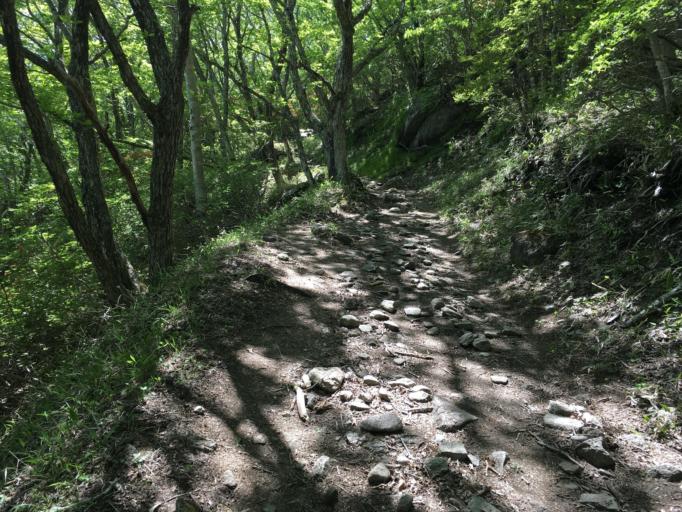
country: JP
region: Iwate
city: Ofunato
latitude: 39.1833
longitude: 141.7372
